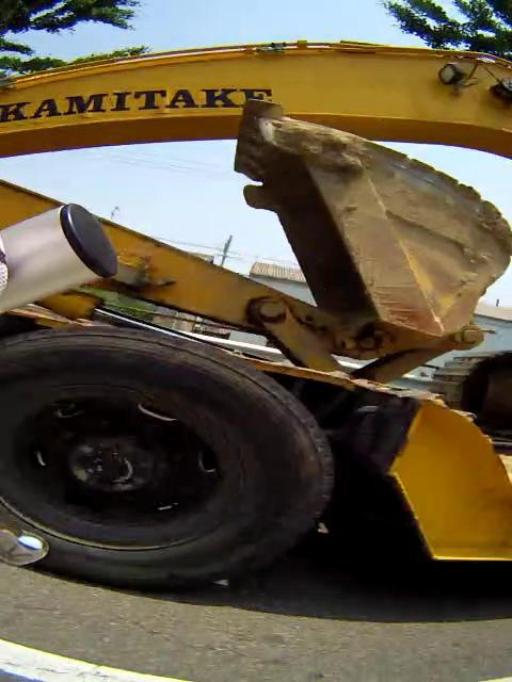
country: JP
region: Osaka
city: Mino
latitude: 34.8292
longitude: 135.4889
